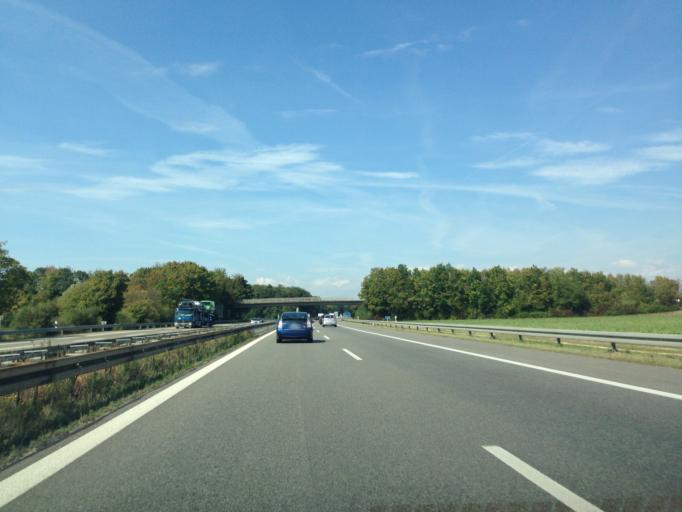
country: DE
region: Bavaria
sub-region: Swabia
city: Senden
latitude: 48.3379
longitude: 10.0319
